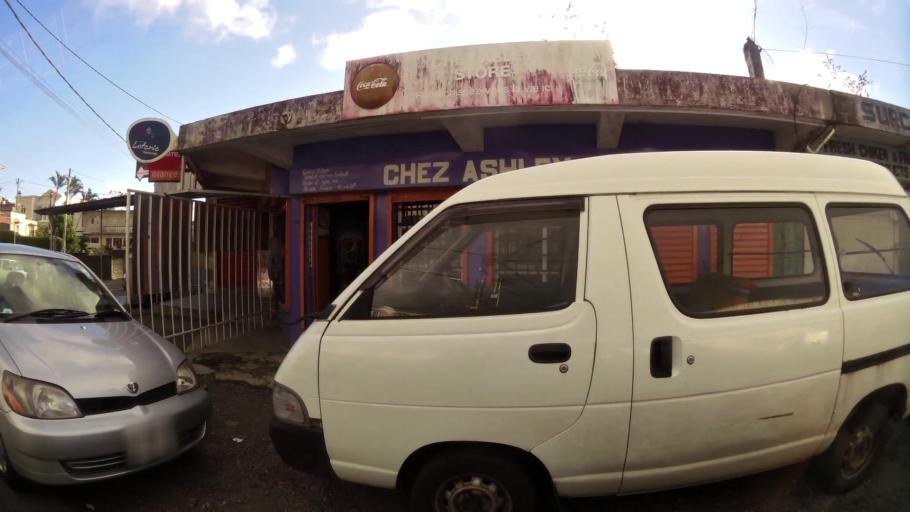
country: MU
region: Plaines Wilhems
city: Curepipe
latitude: -20.3049
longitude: 57.5325
